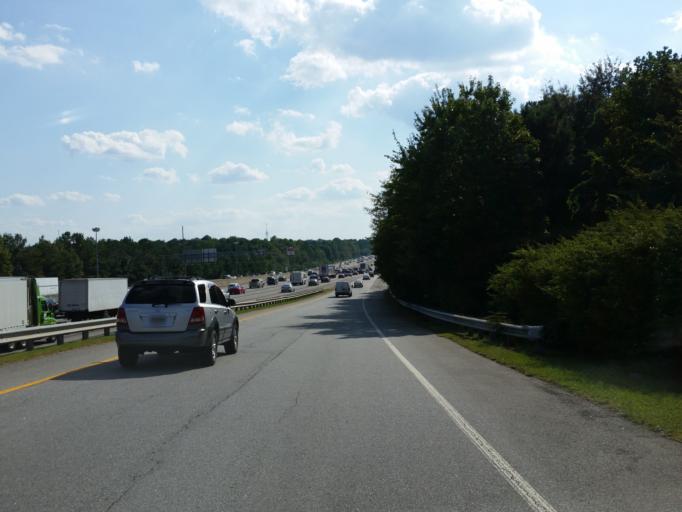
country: US
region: Georgia
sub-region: Gwinnett County
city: Duluth
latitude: 33.9477
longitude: -84.1404
